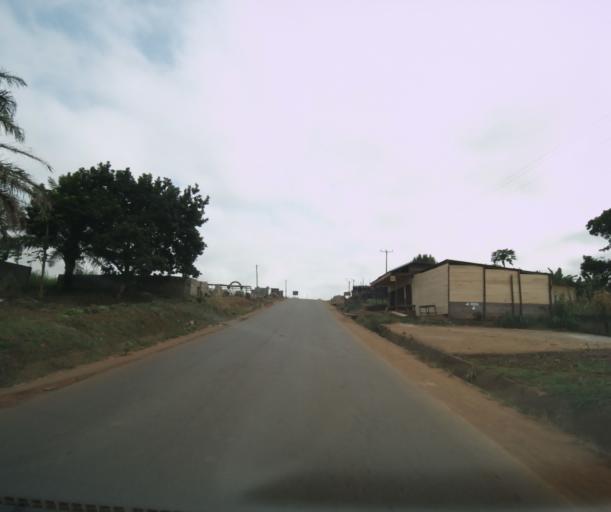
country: CM
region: Centre
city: Yaounde
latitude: 3.8006
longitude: 11.5222
